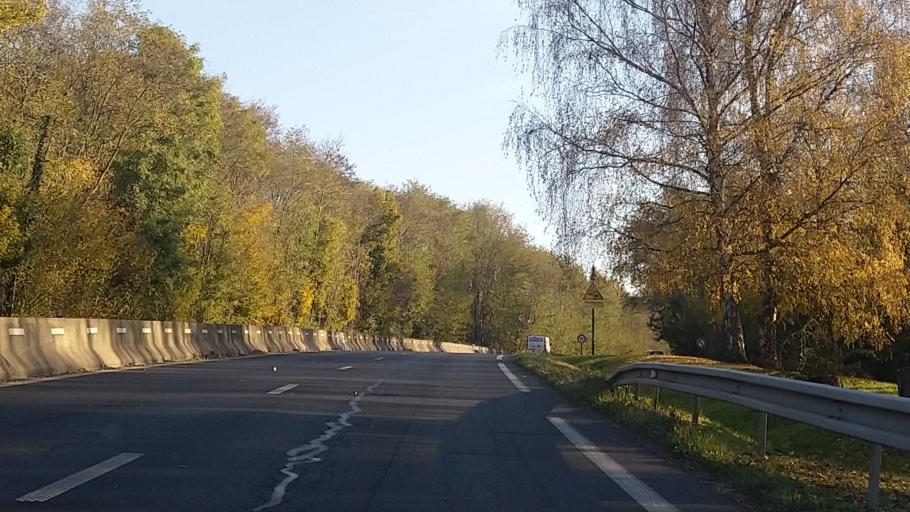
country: FR
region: Ile-de-France
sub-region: Departement du Val-d'Oise
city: Saint-Brice-sous-Foret
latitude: 49.0054
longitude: 2.3563
